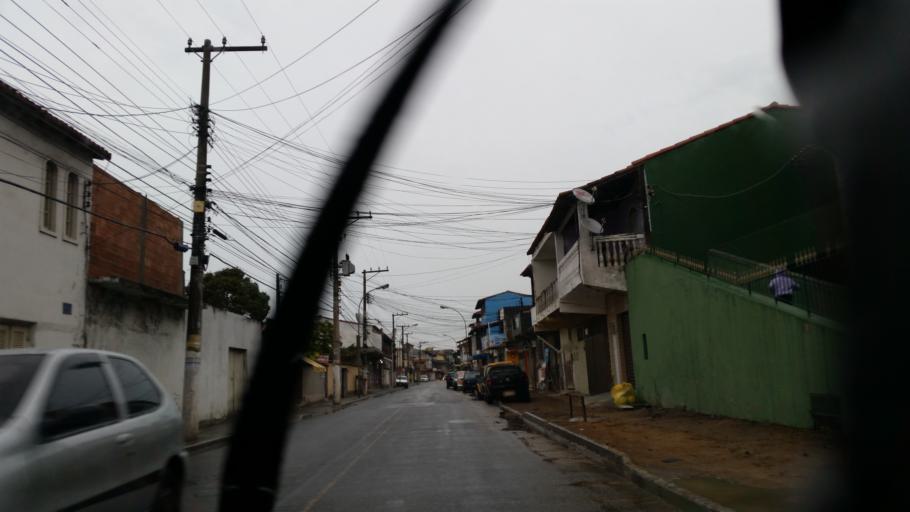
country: BR
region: Rio de Janeiro
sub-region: Cabo Frio
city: Cabo Frio
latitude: -22.8699
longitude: -42.0158
